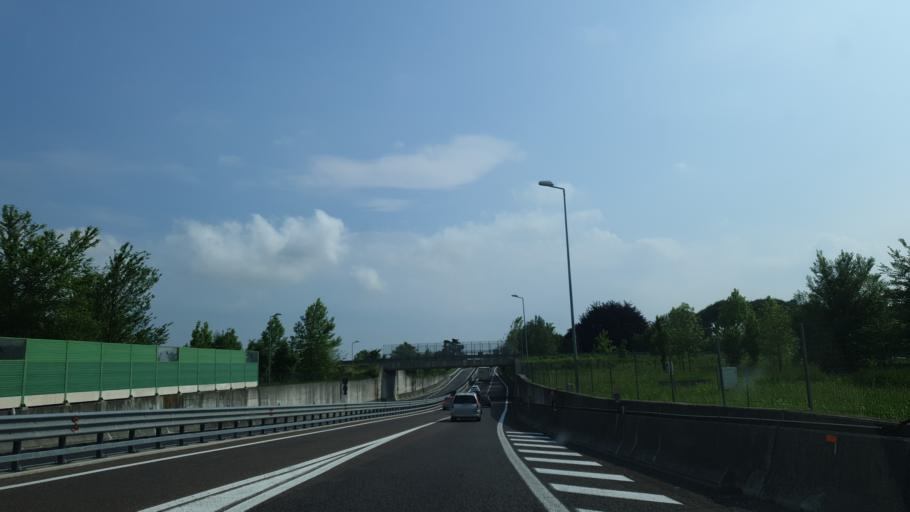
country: IT
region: Veneto
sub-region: Provincia di Venezia
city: Marcon-Gaggio-Colmello
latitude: 45.5863
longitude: 12.2897
